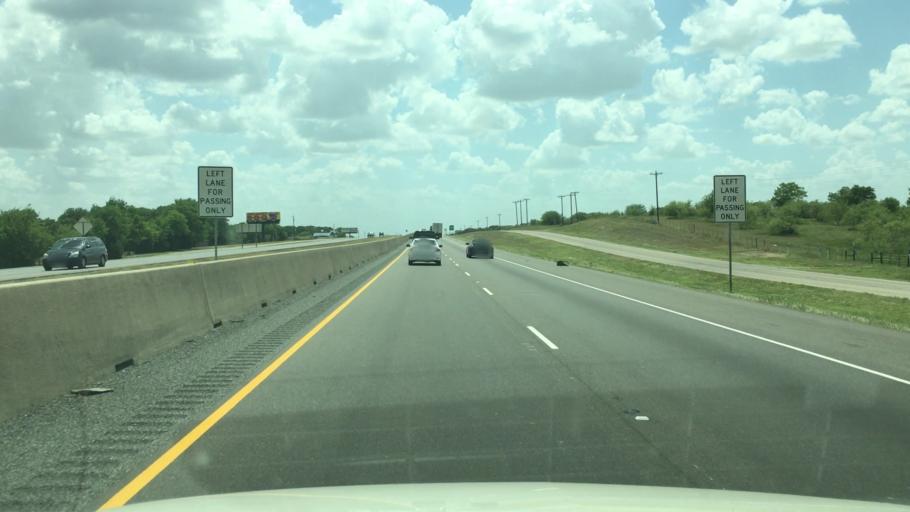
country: US
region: Texas
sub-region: Hunt County
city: Caddo Mills
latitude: 33.0132
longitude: -96.2152
